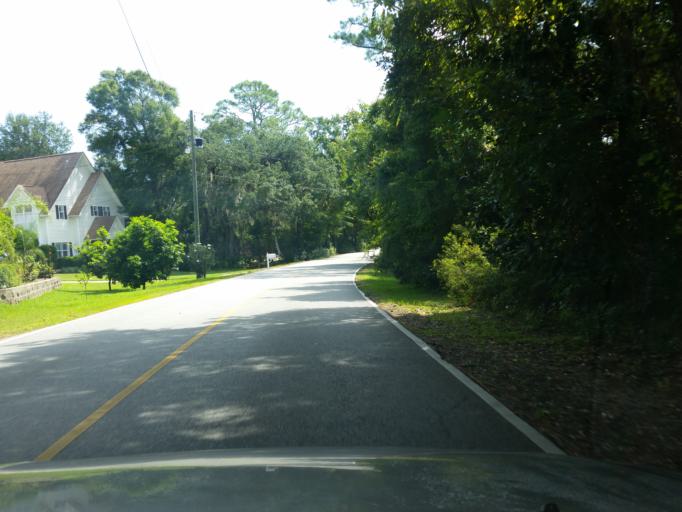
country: US
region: Alabama
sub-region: Baldwin County
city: Orange Beach
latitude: 30.3159
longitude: -87.4838
